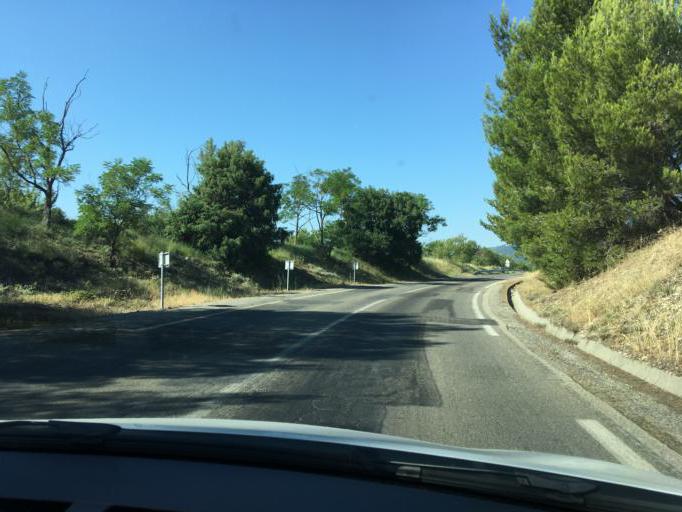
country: FR
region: Provence-Alpes-Cote d'Azur
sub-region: Departement des Alpes-de-Haute-Provence
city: Peyruis
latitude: 44.0387
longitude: 5.9586
